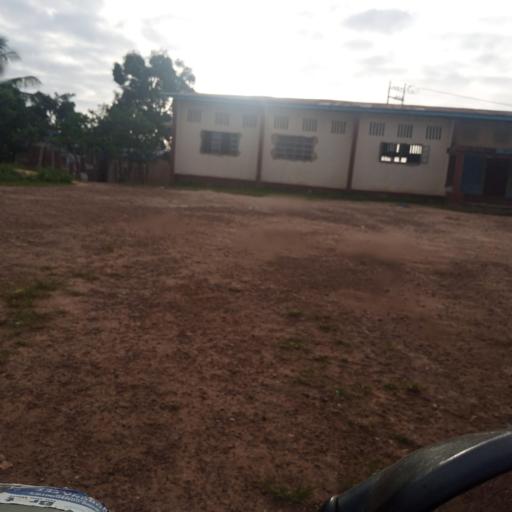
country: SL
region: Eastern Province
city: Pendembu
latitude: 8.0977
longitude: -10.6903
